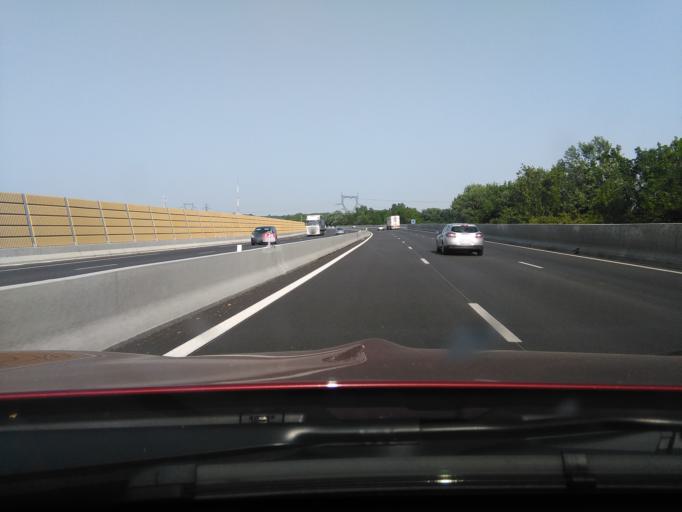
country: FR
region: Rhone-Alpes
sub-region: Departement de l'Ain
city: Massieux
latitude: 45.9025
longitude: 4.8111
